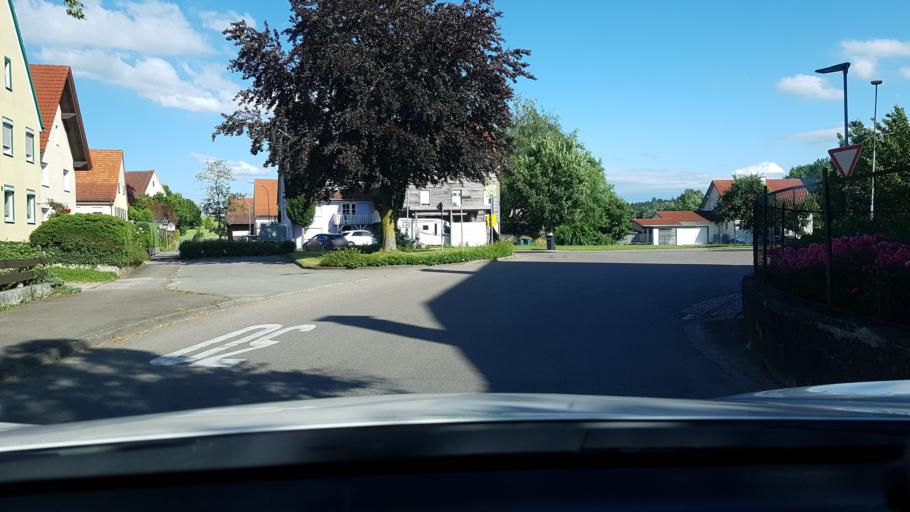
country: DE
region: Baden-Wuerttemberg
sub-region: Tuebingen Region
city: Mietingen
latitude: 48.1814
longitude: 9.9074
